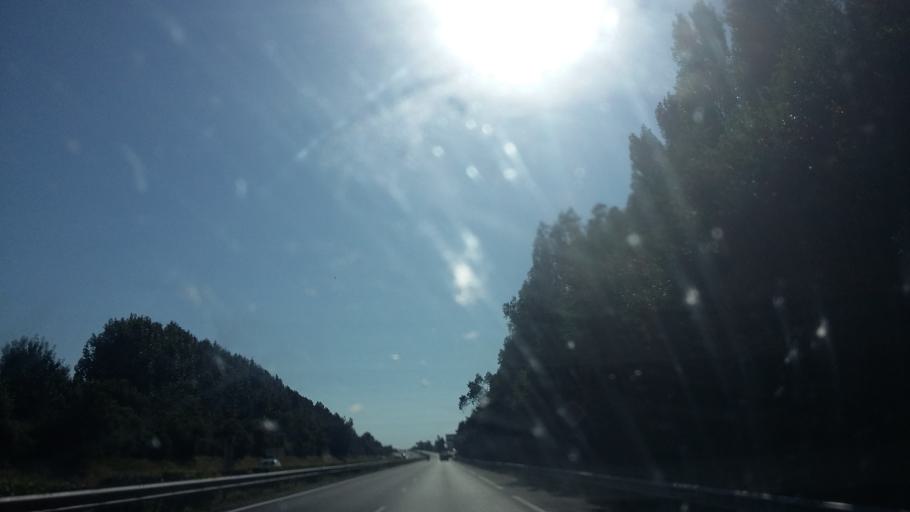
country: FR
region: Pays de la Loire
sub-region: Departement de la Vendee
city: Challans
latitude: 46.8571
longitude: -1.8856
